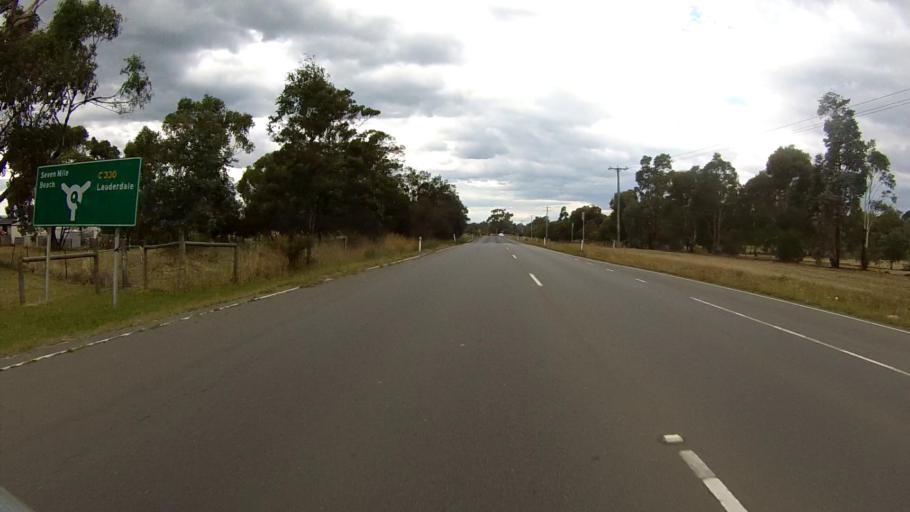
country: AU
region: Tasmania
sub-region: Clarence
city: Cambridge
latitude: -42.8440
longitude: 147.4751
